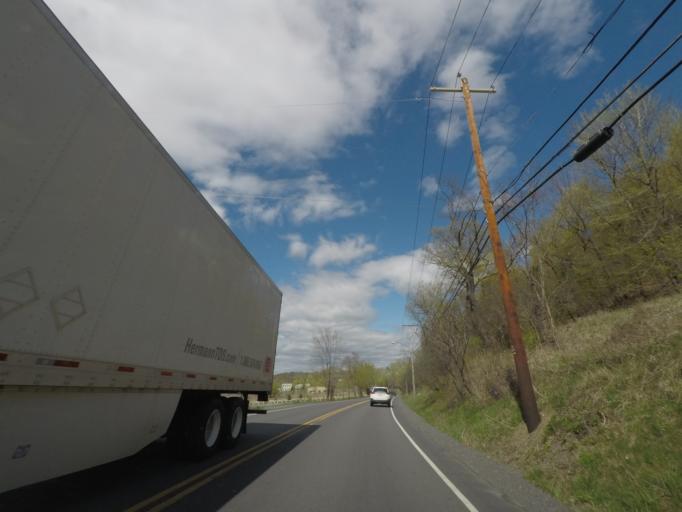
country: US
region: New York
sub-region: Columbia County
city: Oakdale
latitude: 42.2279
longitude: -73.7851
